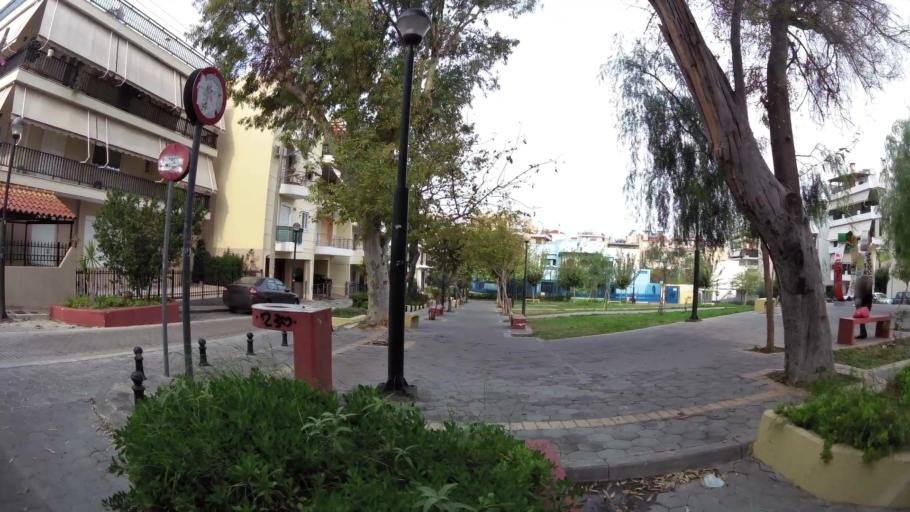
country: GR
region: Attica
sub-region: Nomarchia Athinas
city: Agios Dimitrios
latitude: 37.9329
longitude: 23.7263
